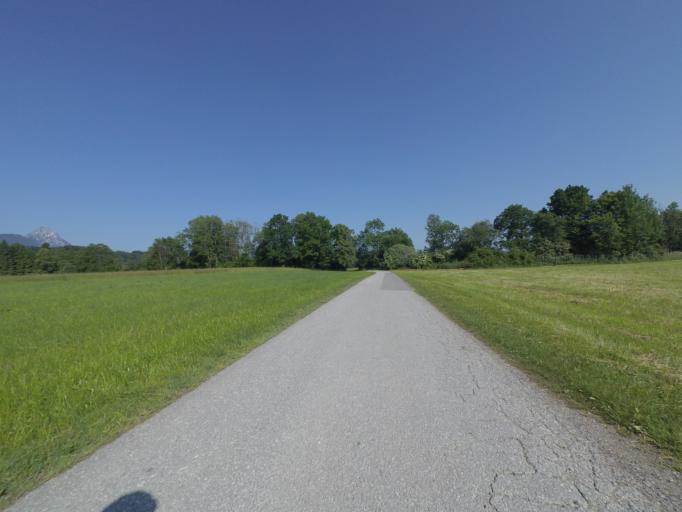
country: DE
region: Bavaria
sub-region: Upper Bavaria
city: Piding
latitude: 47.7633
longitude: 12.9753
